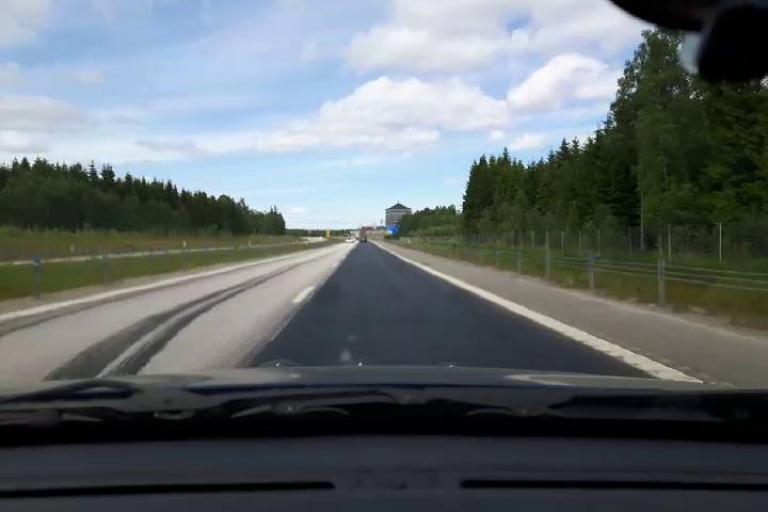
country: SE
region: Uppsala
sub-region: Alvkarleby Kommun
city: AElvkarleby
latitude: 60.4556
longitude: 17.4152
